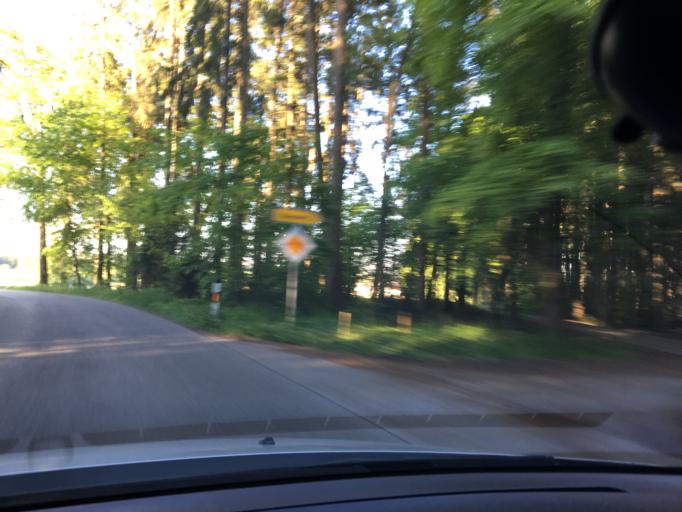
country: DE
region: Bavaria
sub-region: Lower Bavaria
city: Vilsbiburg
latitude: 48.4856
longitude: 12.3764
